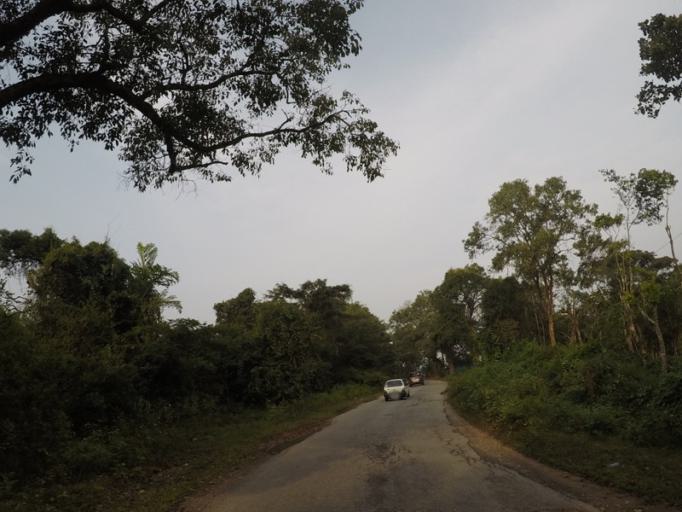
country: IN
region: Karnataka
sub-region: Chikmagalur
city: Chikmagalur
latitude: 13.2668
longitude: 75.6901
